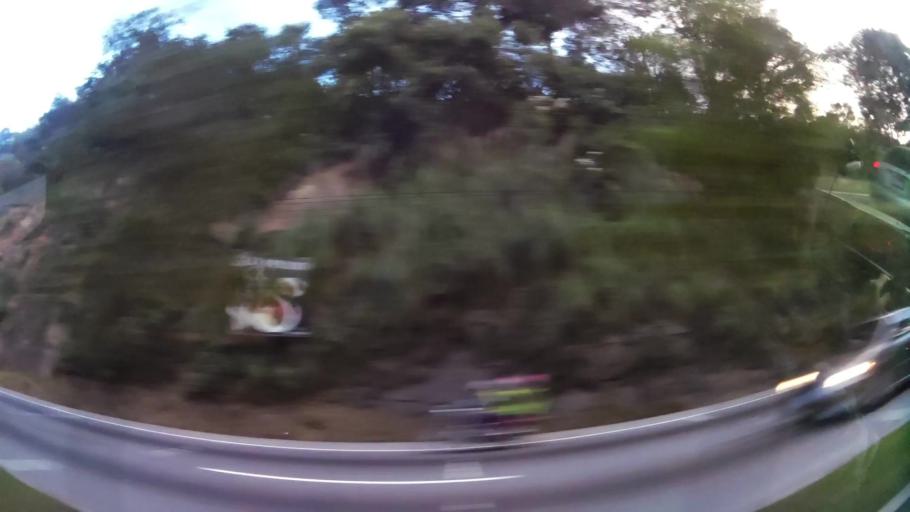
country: GT
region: Sacatepequez
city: San Lucas Sacatepequez
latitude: 14.6108
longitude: -90.6501
